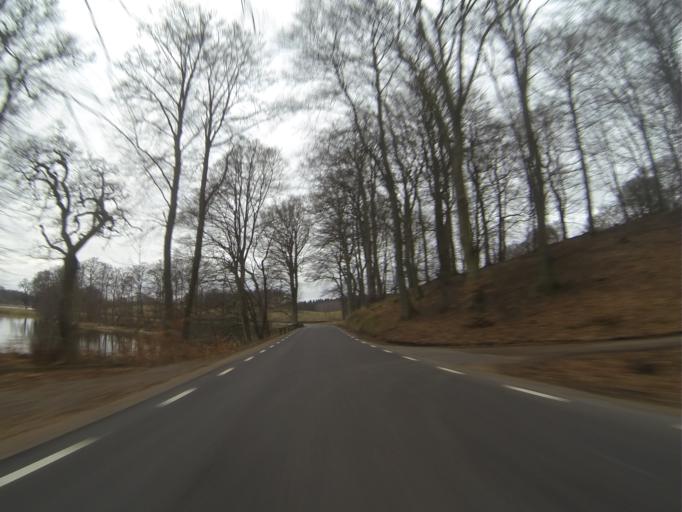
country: SE
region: Skane
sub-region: Lunds Kommun
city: Genarp
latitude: 55.5790
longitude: 13.4326
